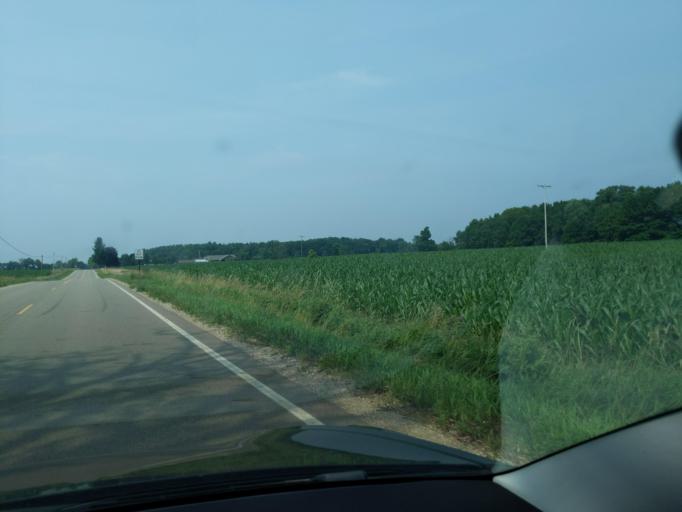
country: US
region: Michigan
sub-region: Clinton County
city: DeWitt
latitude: 42.8613
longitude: -84.5724
